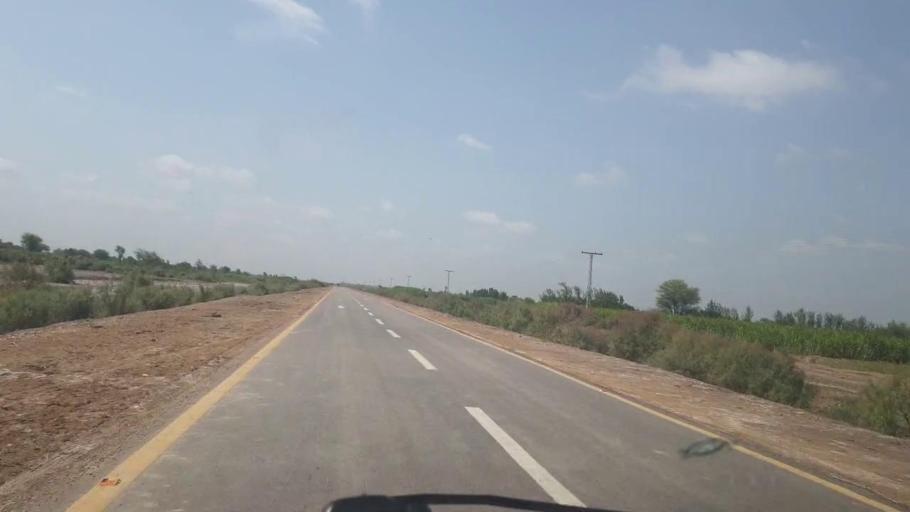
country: PK
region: Sindh
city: Berani
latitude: 25.7310
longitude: 68.9443
